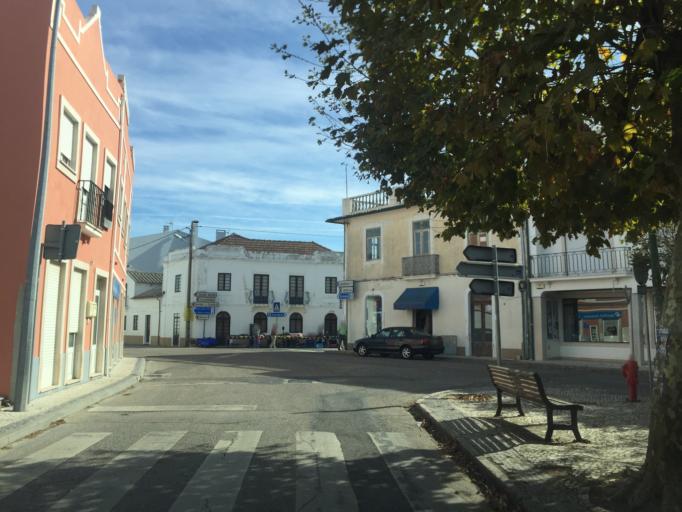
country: PT
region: Coimbra
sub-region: Figueira da Foz
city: Lavos
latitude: 40.0697
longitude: -8.8072
